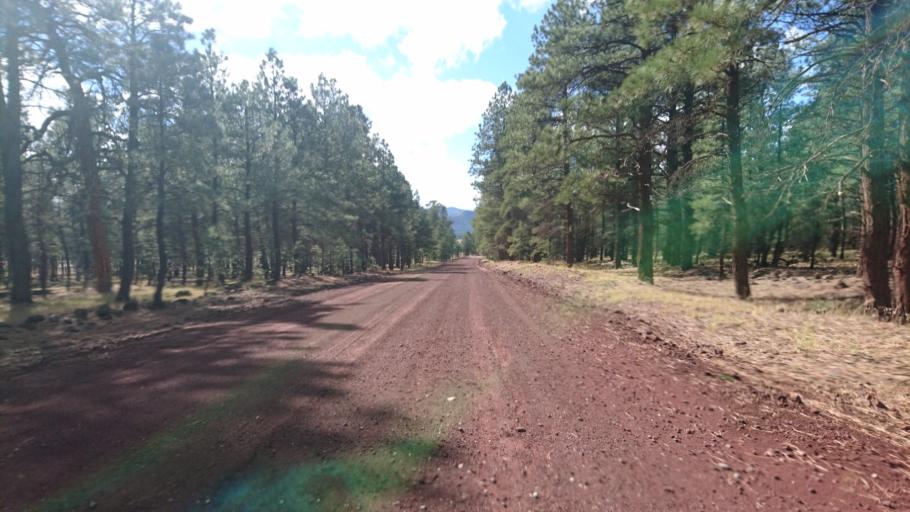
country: US
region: Arizona
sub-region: Coconino County
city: Williams
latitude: 35.2599
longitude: -112.1090
